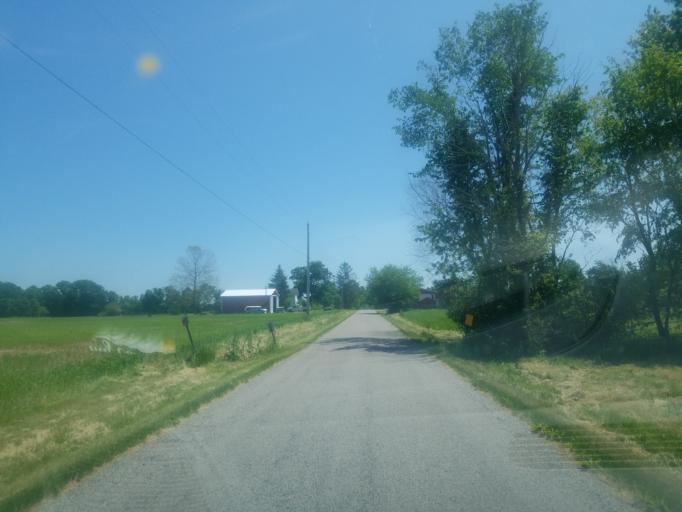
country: US
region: Ohio
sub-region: Huron County
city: New London
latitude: 41.1379
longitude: -82.3587
